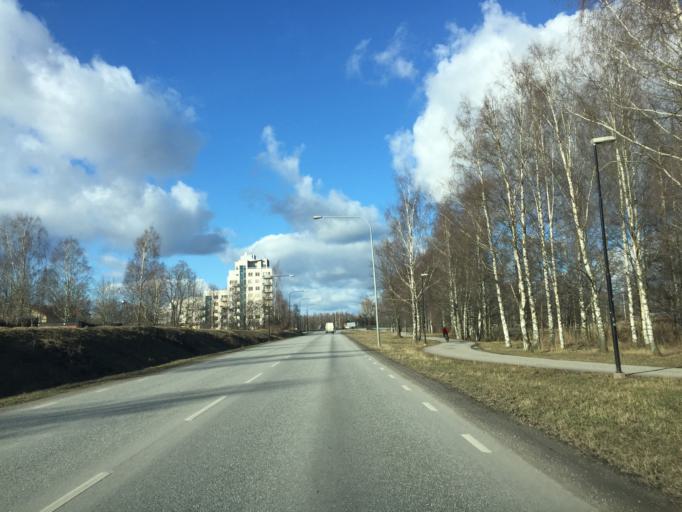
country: SE
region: OErebro
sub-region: Orebro Kommun
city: Orebro
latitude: 59.2702
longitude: 15.2411
